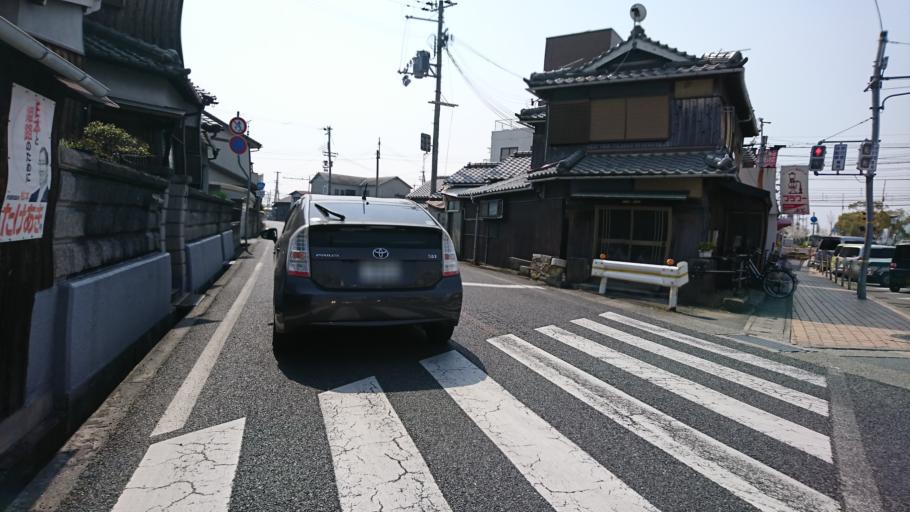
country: JP
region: Hyogo
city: Shirahamacho-usazakiminami
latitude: 34.7796
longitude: 134.7583
